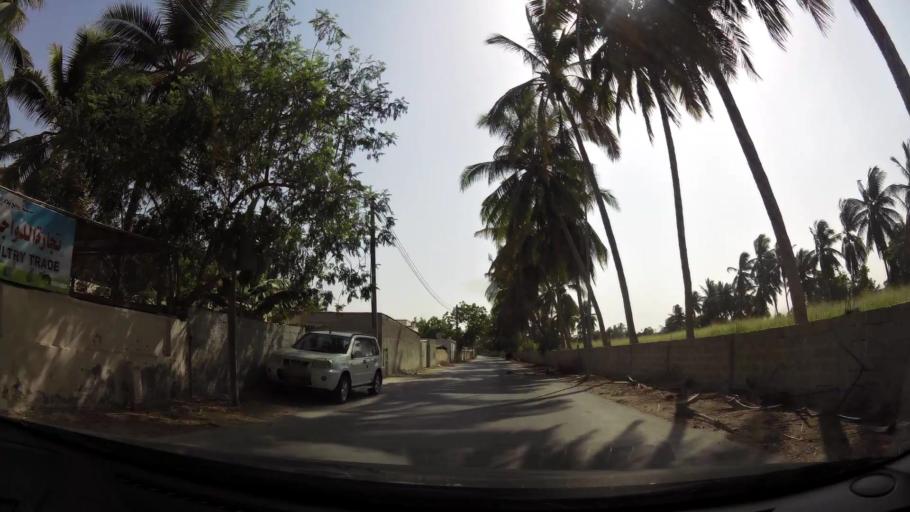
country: OM
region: Zufar
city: Salalah
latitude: 17.0033
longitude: 54.0567
